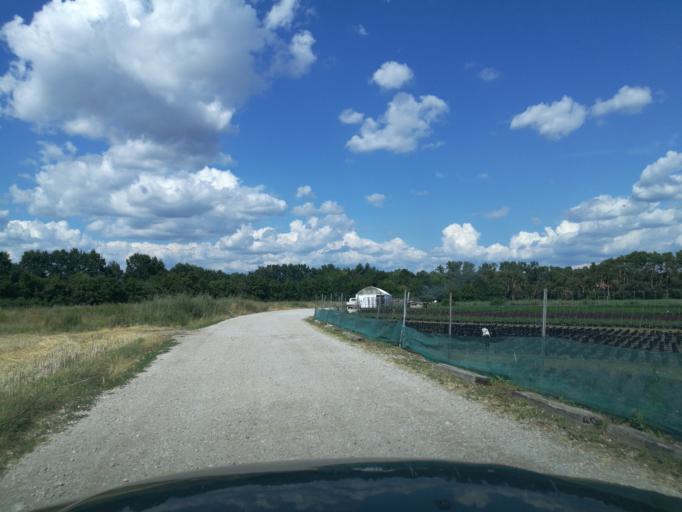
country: DE
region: Bavaria
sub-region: Regierungsbezirk Mittelfranken
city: Furth
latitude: 49.4933
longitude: 10.9560
